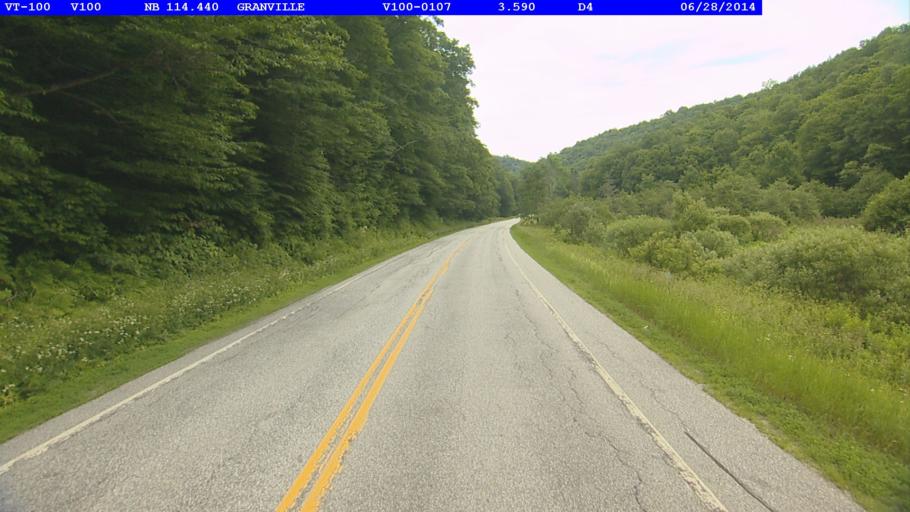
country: US
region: Vermont
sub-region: Orange County
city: Randolph
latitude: 43.9931
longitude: -72.8526
